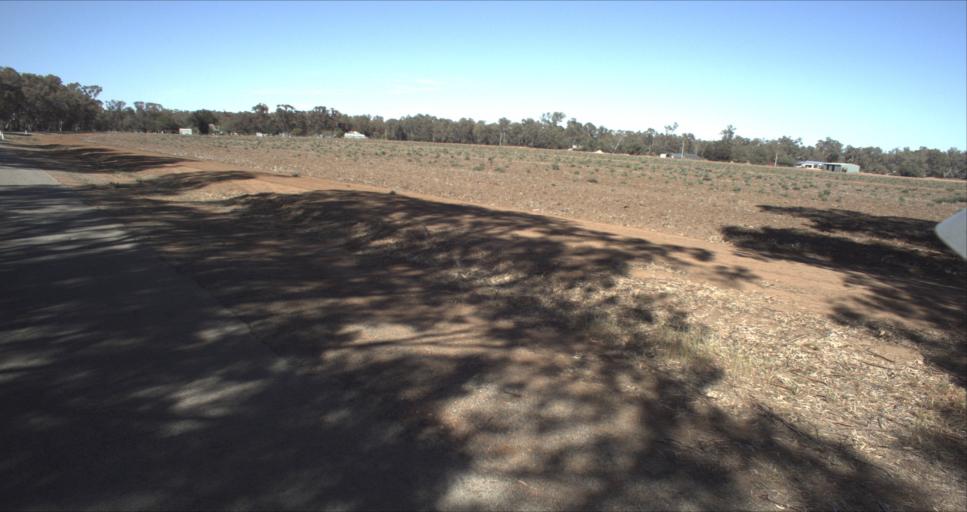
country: AU
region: New South Wales
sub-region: Leeton
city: Leeton
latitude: -34.6109
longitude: 146.2599
